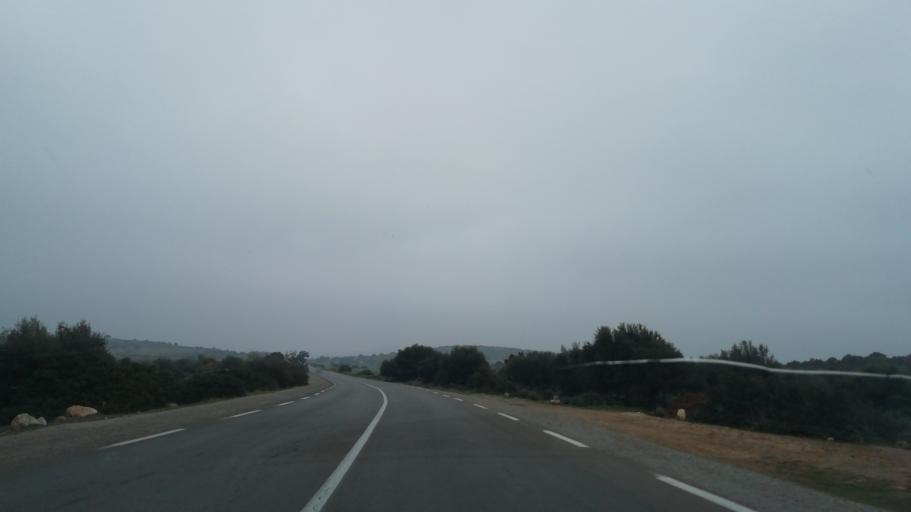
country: DZ
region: Mascara
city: Oued el Abtal
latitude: 35.2984
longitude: 0.4486
